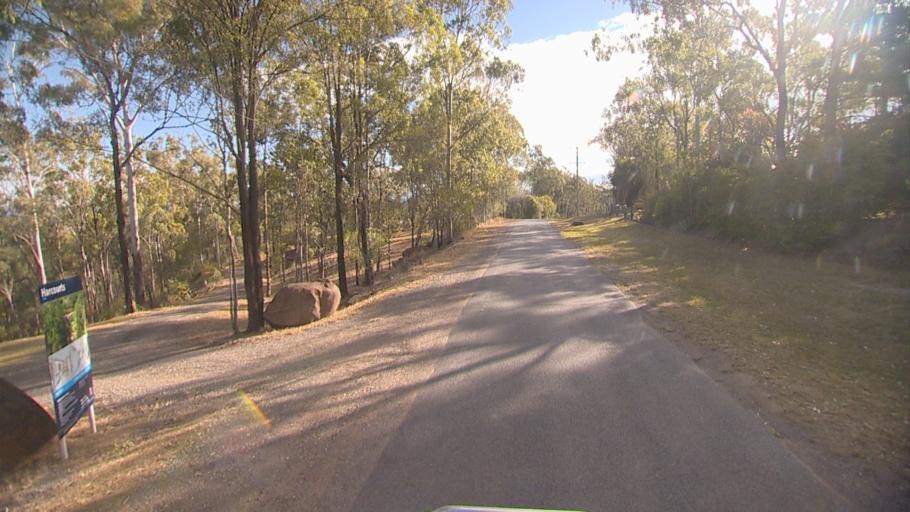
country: AU
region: Queensland
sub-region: Logan
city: Cedar Vale
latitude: -27.8488
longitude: 153.0717
